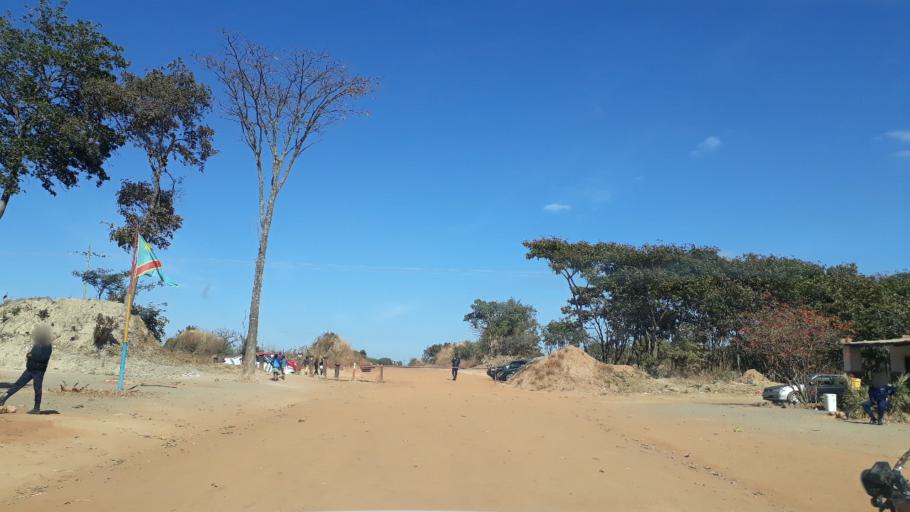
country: ZM
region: Copperbelt
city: Ndola
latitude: -12.8545
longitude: 28.5409
